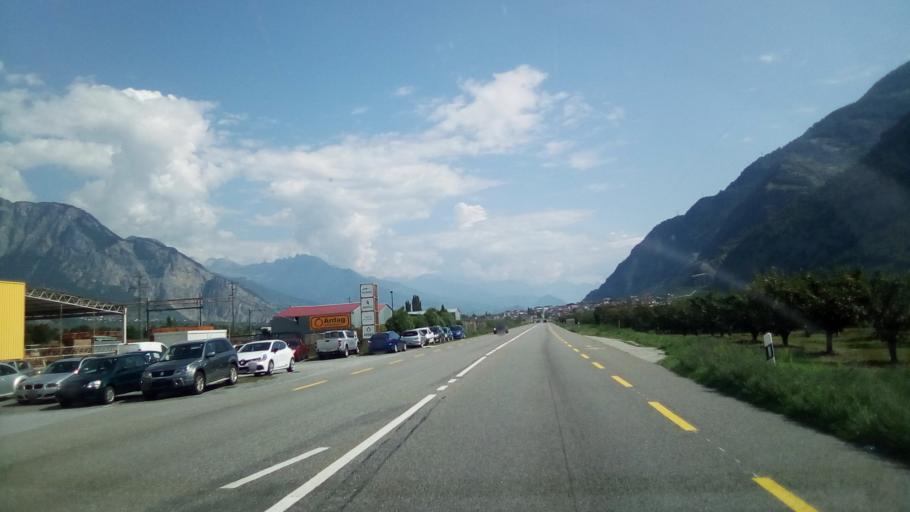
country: CH
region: Valais
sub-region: Martigny District
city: Saillon
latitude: 46.1613
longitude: 7.1998
